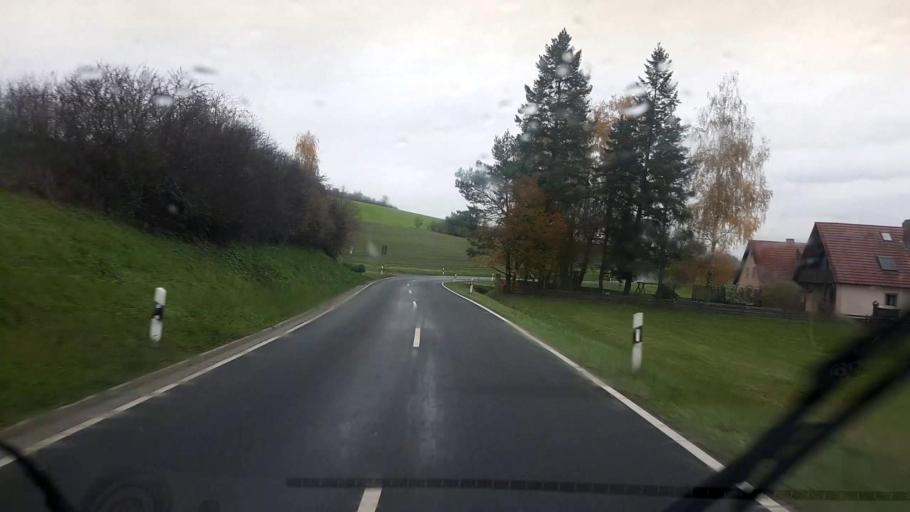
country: DE
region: Bavaria
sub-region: Upper Franconia
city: Burgwindheim
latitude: 49.8750
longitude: 10.5724
